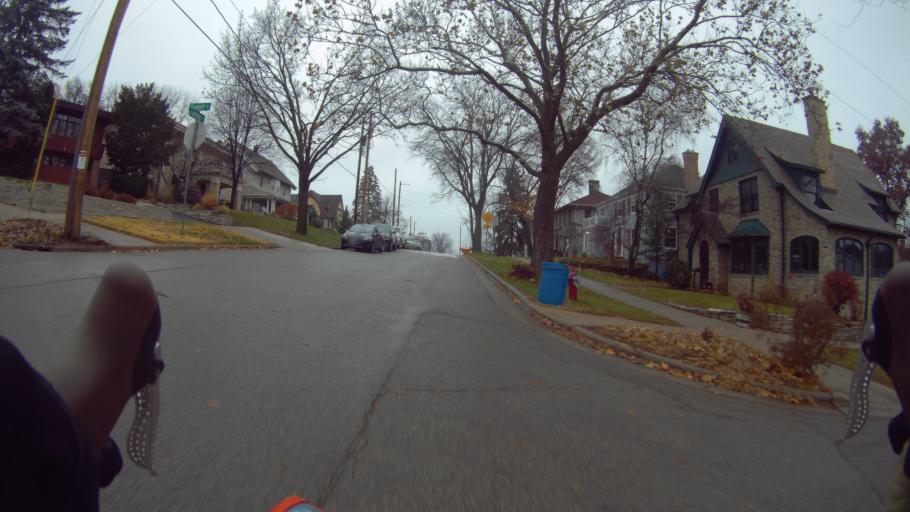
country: US
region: Wisconsin
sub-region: Dane County
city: Madison
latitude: 43.0715
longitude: -89.4151
